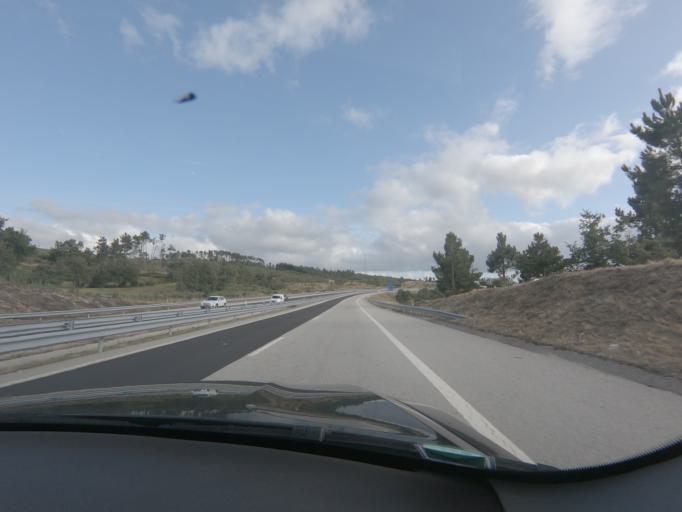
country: PT
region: Viseu
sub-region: Castro Daire
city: Castro Daire
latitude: 40.9855
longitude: -7.8830
